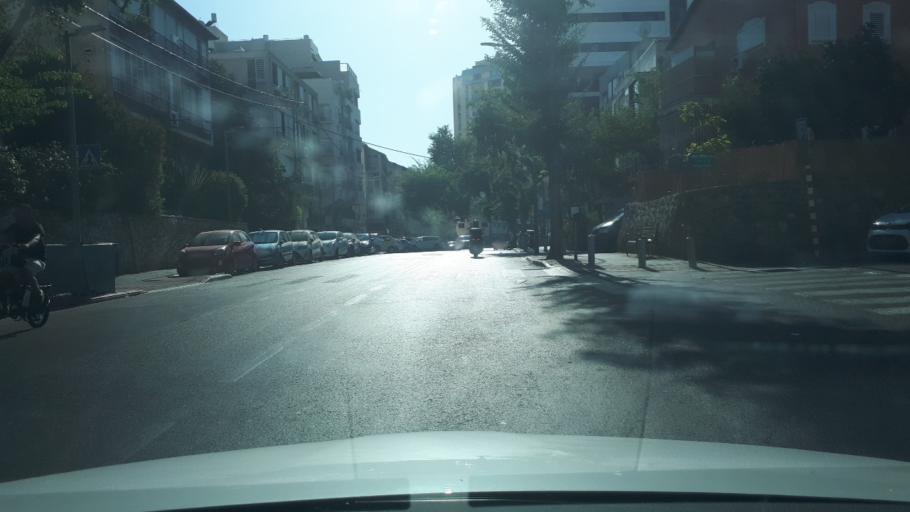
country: IL
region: Tel Aviv
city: Ramat Gan
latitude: 32.0800
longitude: 34.8171
